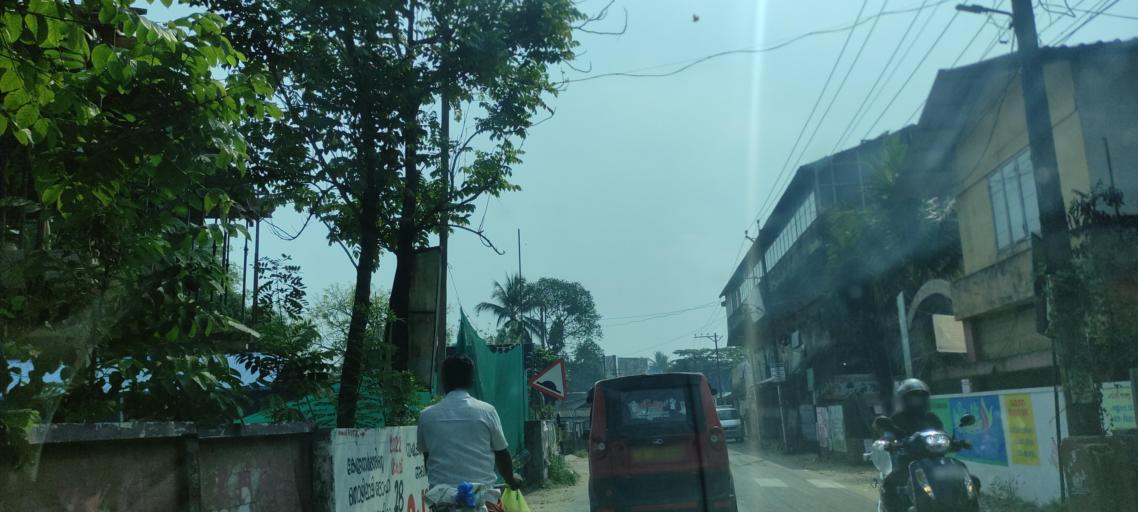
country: IN
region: Kerala
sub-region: Alappuzha
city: Kutiatodu
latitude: 9.8235
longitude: 76.3097
